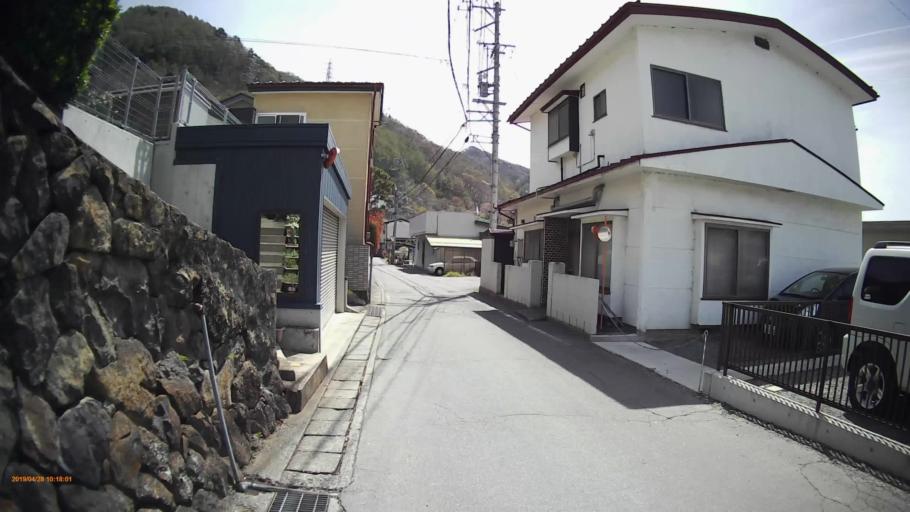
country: JP
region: Nagano
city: Suwa
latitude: 36.0639
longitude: 138.1093
